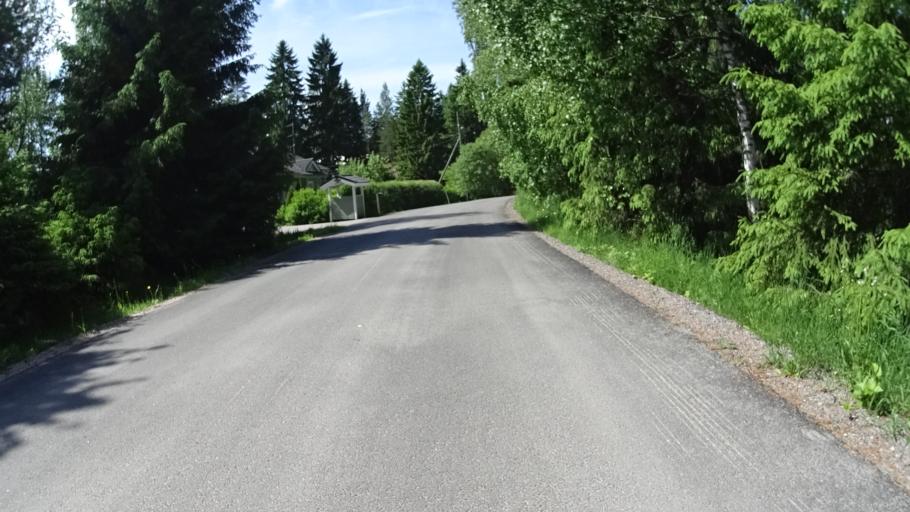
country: FI
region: Uusimaa
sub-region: Helsinki
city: Kauniainen
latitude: 60.3204
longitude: 24.7308
